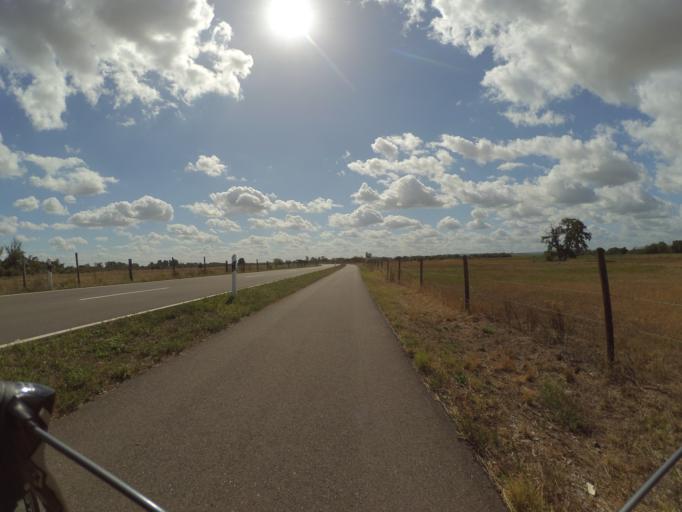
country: DE
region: North Rhine-Westphalia
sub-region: Regierungsbezirk Koln
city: Inden
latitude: 50.8915
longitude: 6.3742
